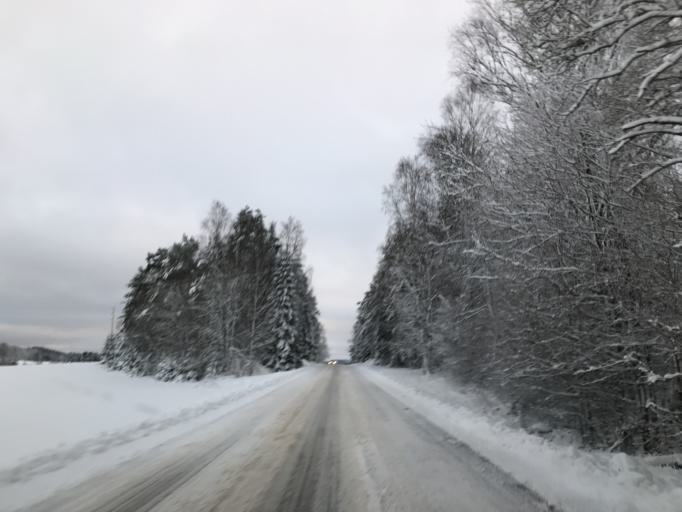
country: SE
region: Vaestra Goetaland
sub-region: Svenljunga Kommun
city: Svenljunga
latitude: 57.3201
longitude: 13.0248
